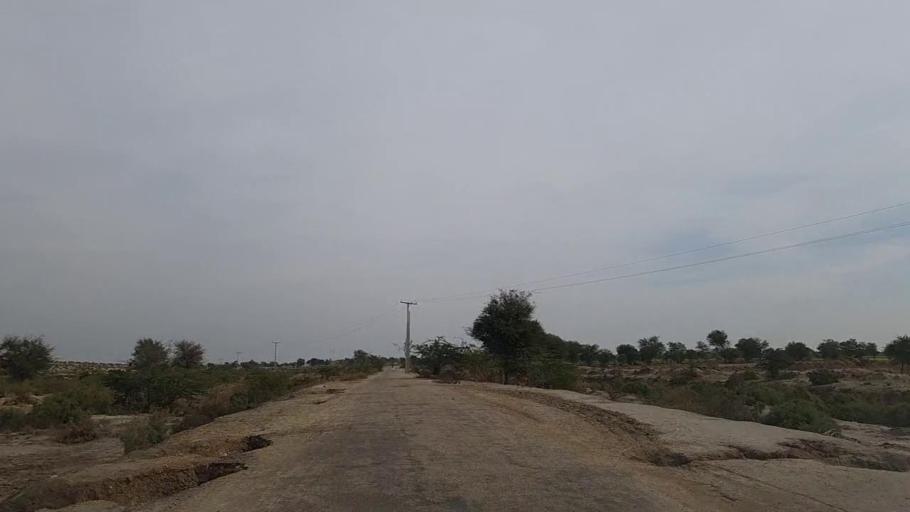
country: PK
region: Sindh
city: Jam Sahib
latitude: 26.4004
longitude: 68.5080
